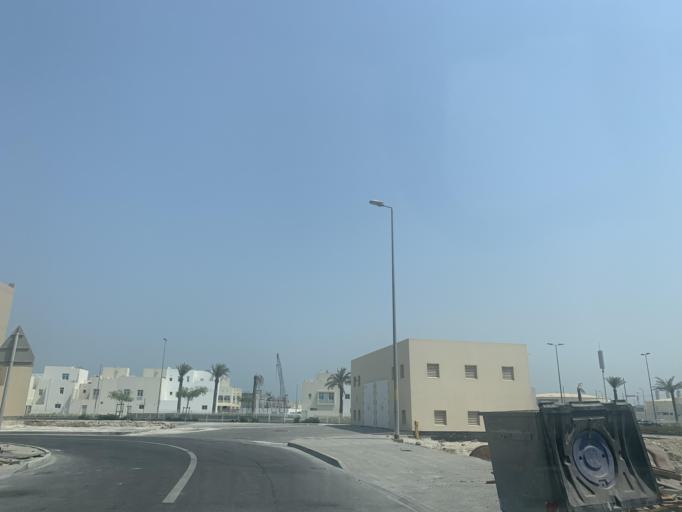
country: BH
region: Muharraq
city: Al Hadd
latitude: 26.2360
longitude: 50.6630
